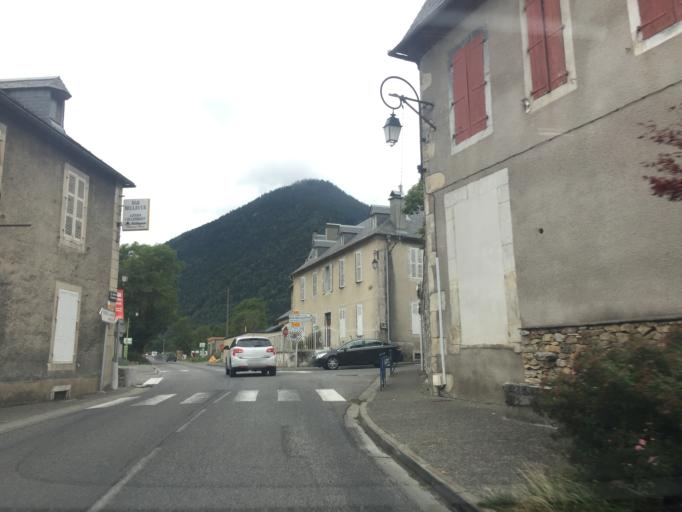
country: FR
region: Midi-Pyrenees
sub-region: Departement des Hautes-Pyrenees
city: Saint-Lary-Soulan
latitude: 42.8722
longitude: 0.3413
